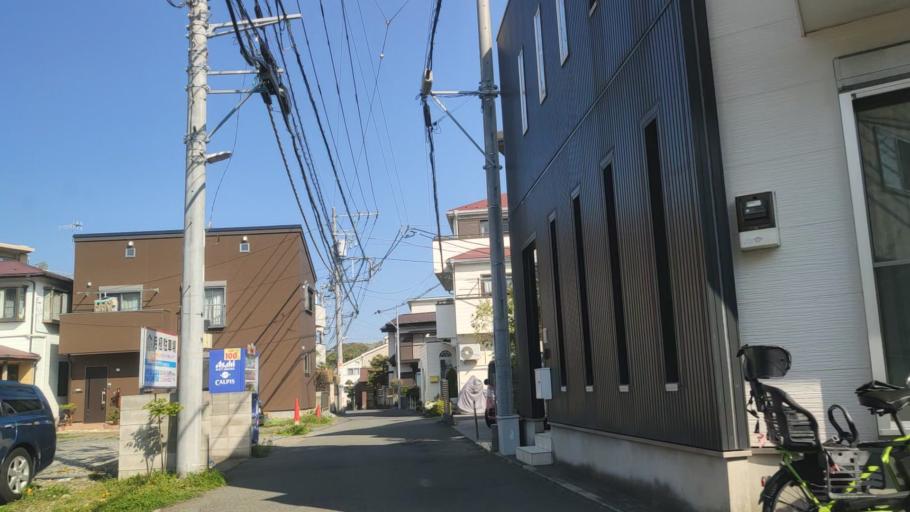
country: JP
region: Kanagawa
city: Fujisawa
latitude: 35.3428
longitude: 139.4433
